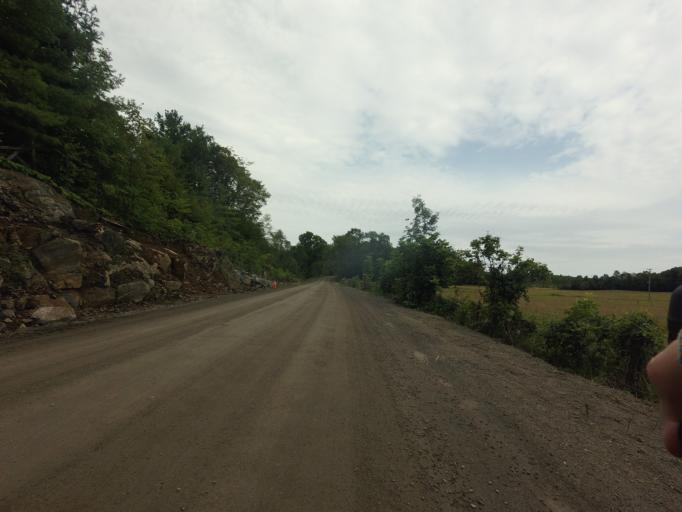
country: CA
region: Ontario
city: Kingston
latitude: 44.5864
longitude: -76.6361
